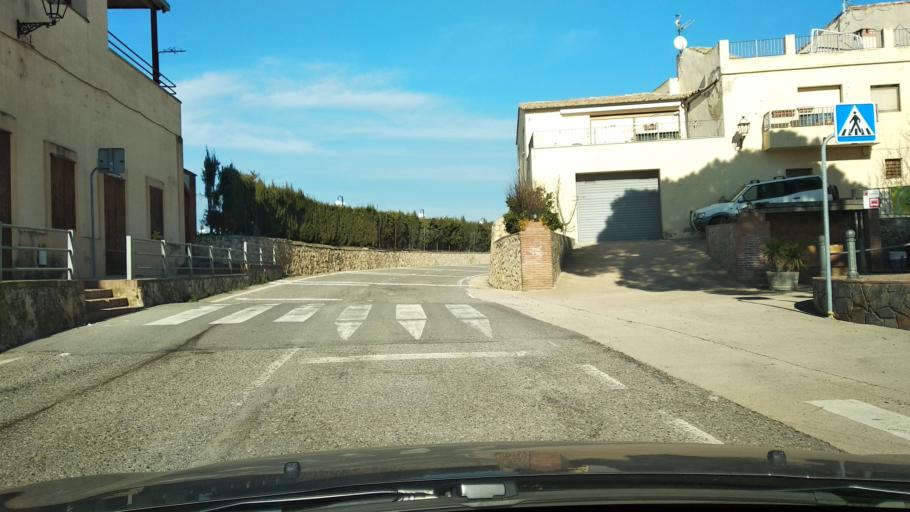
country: ES
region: Catalonia
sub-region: Provincia de Tarragona
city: Falset
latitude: 41.1924
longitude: 0.7749
